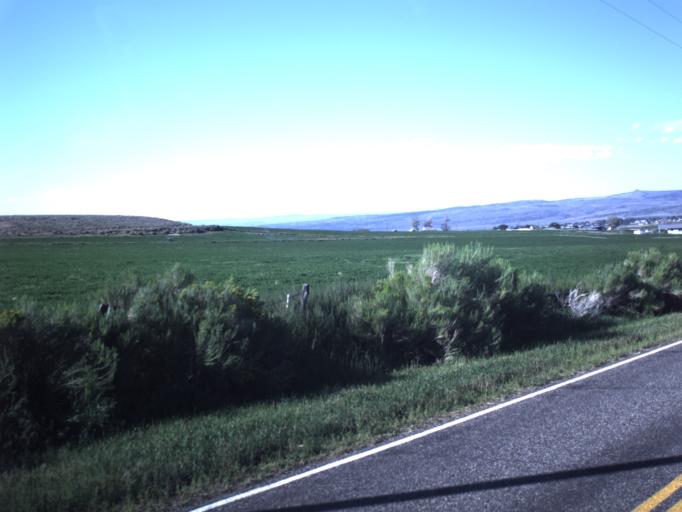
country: US
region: Utah
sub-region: Wayne County
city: Loa
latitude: 38.4399
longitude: -111.6171
